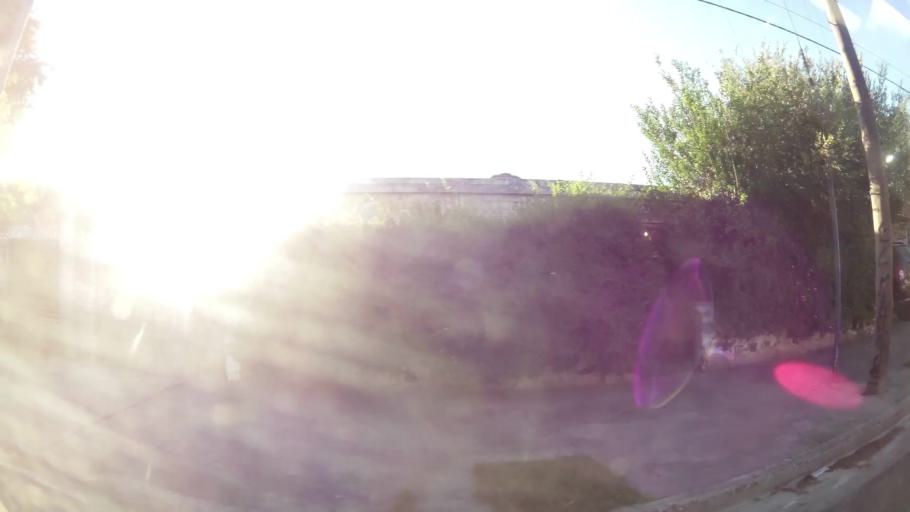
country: AR
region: Cordoba
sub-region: Departamento de Capital
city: Cordoba
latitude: -31.3733
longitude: -64.2002
